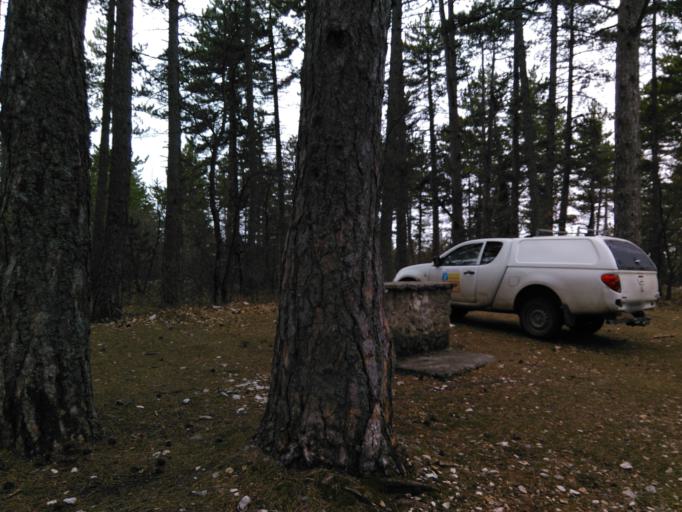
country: FR
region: Provence-Alpes-Cote d'Azur
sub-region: Departement du Vaucluse
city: Villes-sur-Auzon
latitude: 44.1154
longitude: 5.3054
